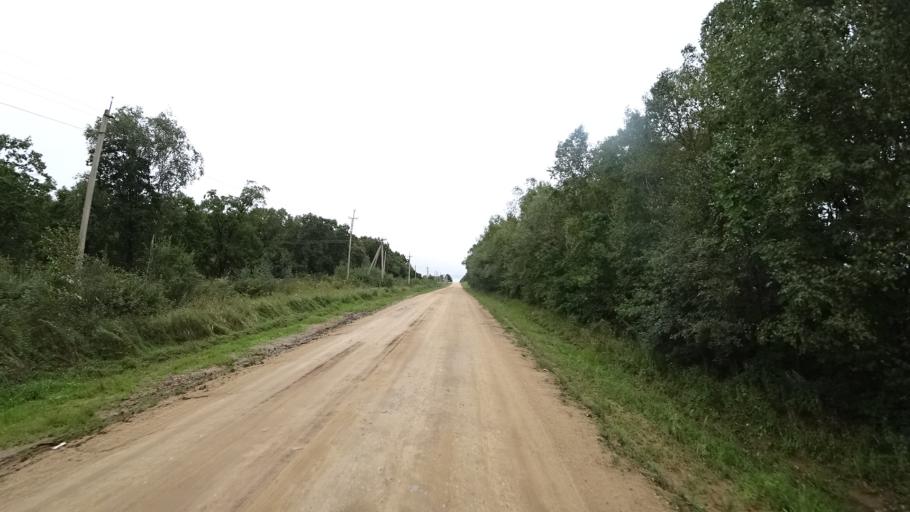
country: RU
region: Primorskiy
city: Ivanovka
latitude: 44.0748
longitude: 132.5855
